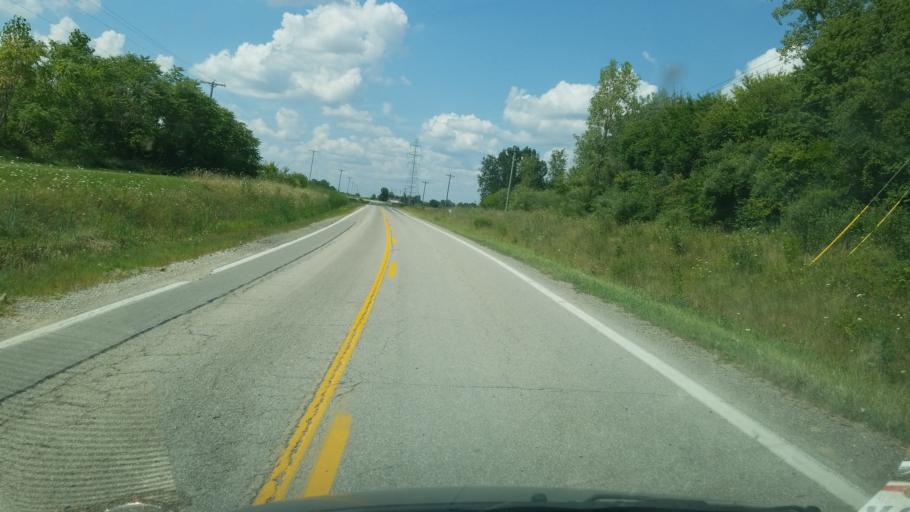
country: US
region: Ohio
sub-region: Union County
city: Richwood
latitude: 40.4163
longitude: -83.4530
